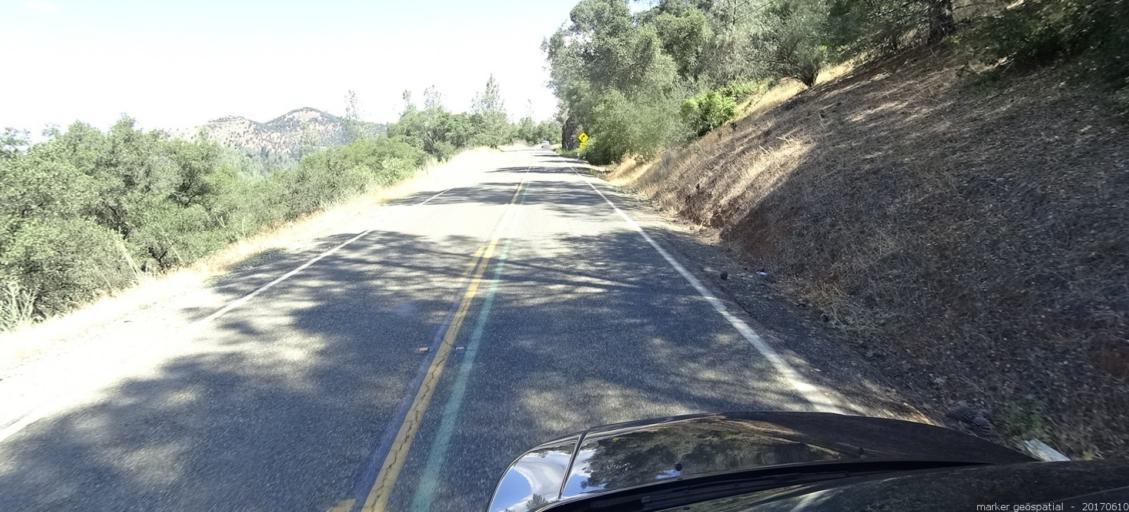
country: US
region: California
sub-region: Butte County
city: Oroville East
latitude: 39.5318
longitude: -121.5080
